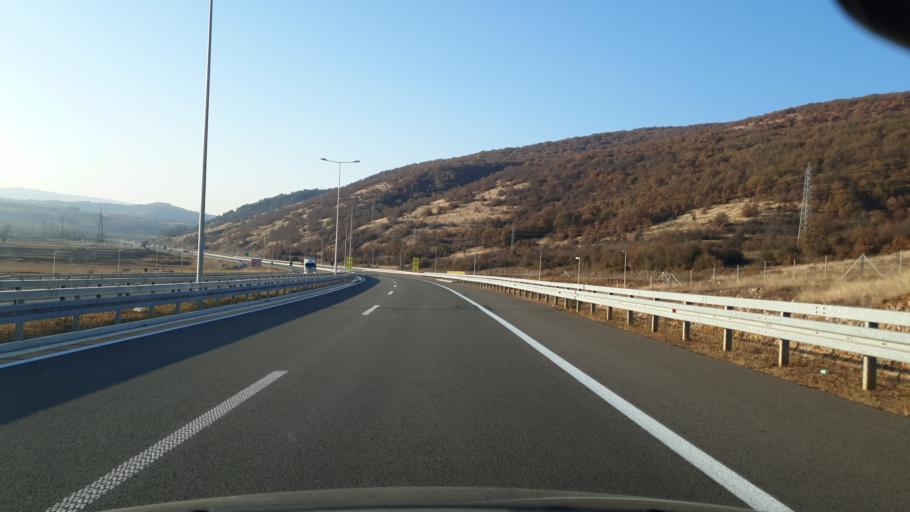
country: RS
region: Central Serbia
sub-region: Pirotski Okrug
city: Dimitrovgrad
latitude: 43.0186
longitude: 22.7478
